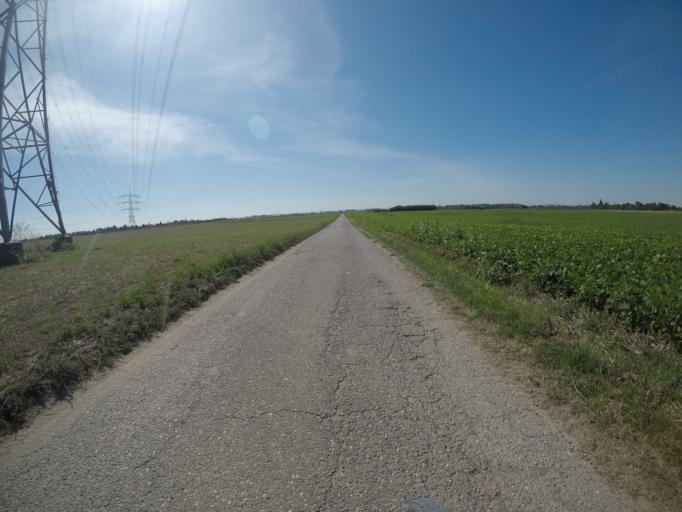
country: DE
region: Hesse
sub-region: Regierungsbezirk Darmstadt
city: Biblis
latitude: 49.6718
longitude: 8.4163
